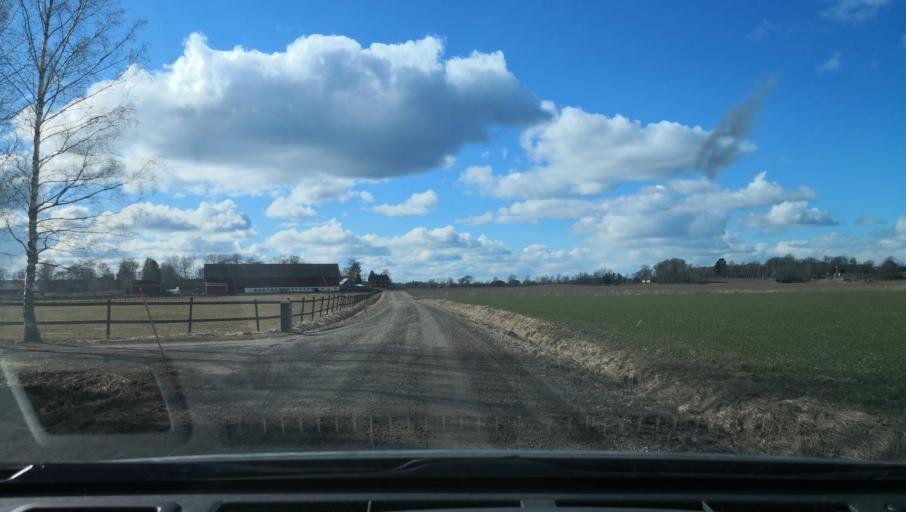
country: SE
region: OErebro
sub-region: Lindesbergs Kommun
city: Fellingsbro
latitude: 59.4136
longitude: 15.6461
